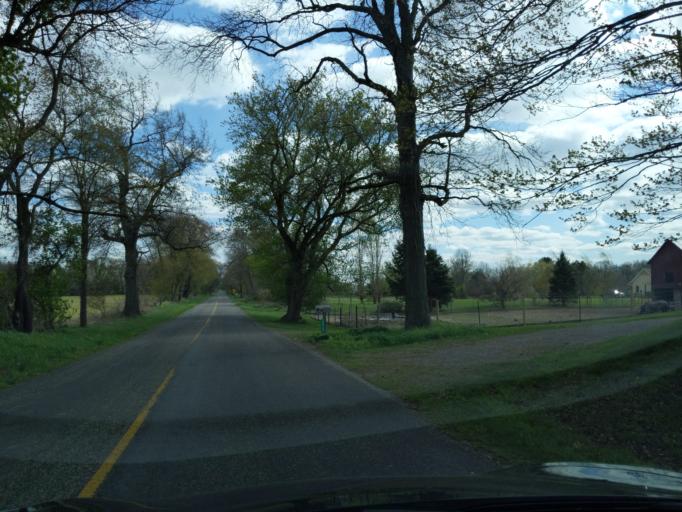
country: US
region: Michigan
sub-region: Ingham County
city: Leslie
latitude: 42.4834
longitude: -84.5412
